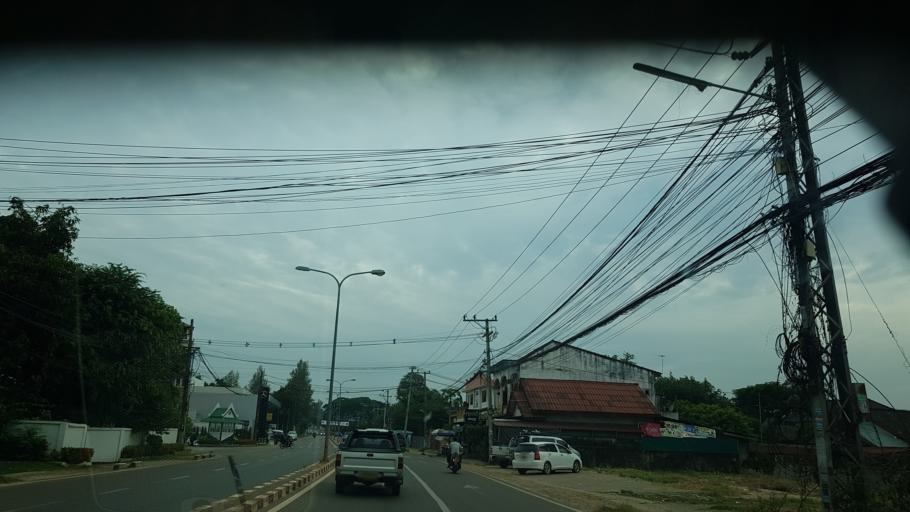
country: LA
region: Vientiane
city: Vientiane
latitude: 17.9429
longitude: 102.6187
